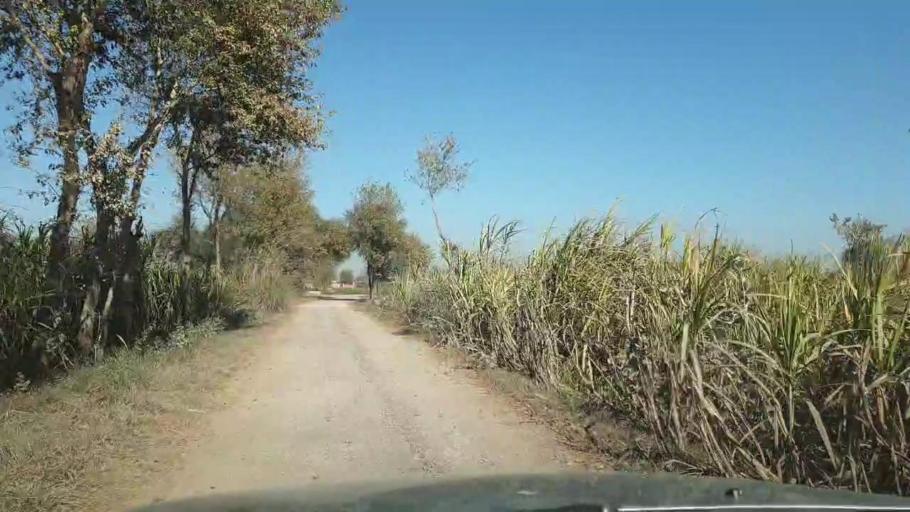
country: PK
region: Sindh
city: Ghotki
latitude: 28.0366
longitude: 69.2774
